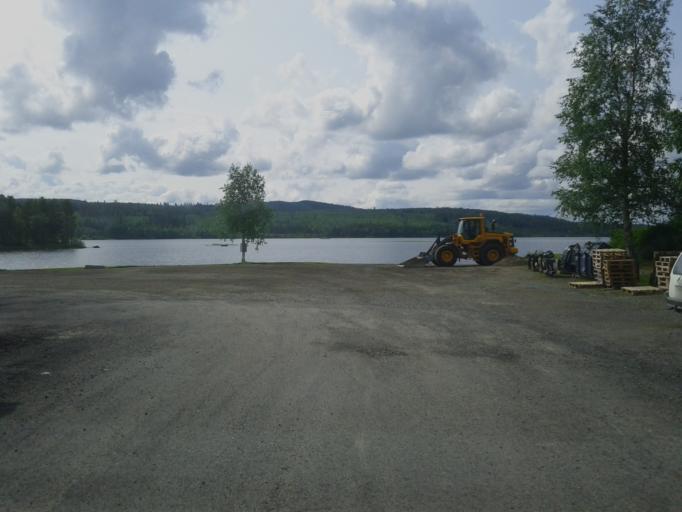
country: SE
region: Vaesterbotten
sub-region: Mala Kommun
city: Mala
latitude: 65.1792
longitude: 18.7463
